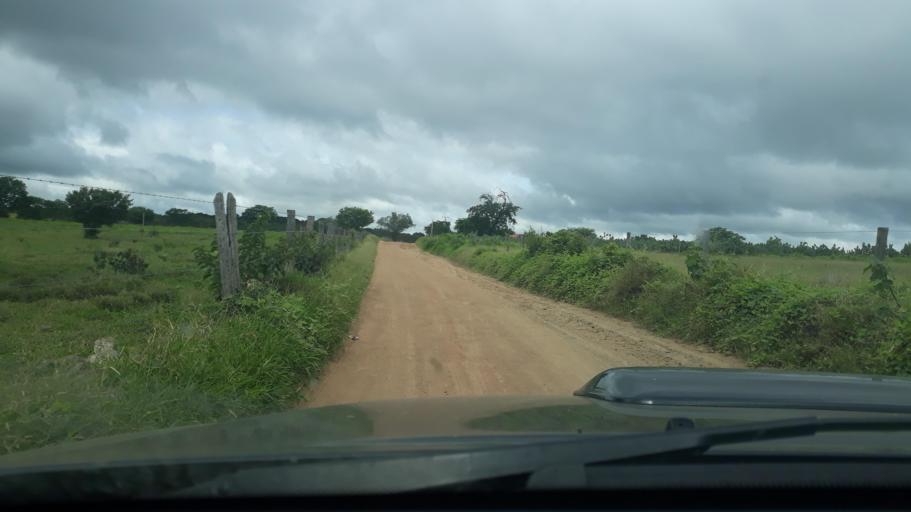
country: BR
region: Bahia
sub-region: Riacho De Santana
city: Riacho de Santana
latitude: -13.8991
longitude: -42.8774
